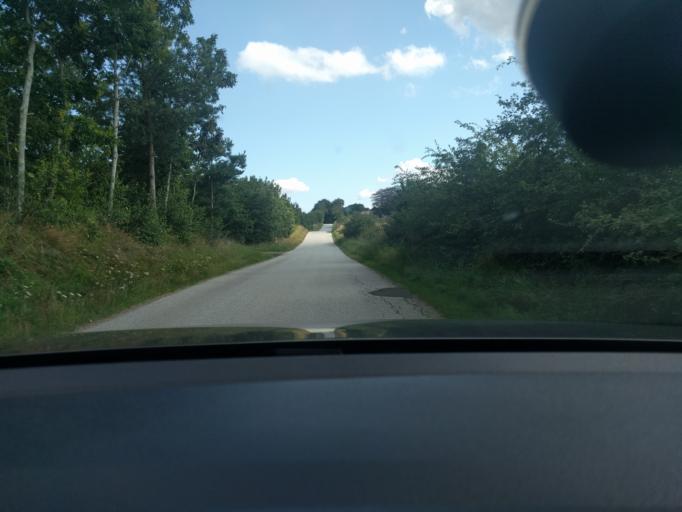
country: DK
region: Central Jutland
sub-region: Viborg Kommune
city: Viborg
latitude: 56.4978
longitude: 9.2922
